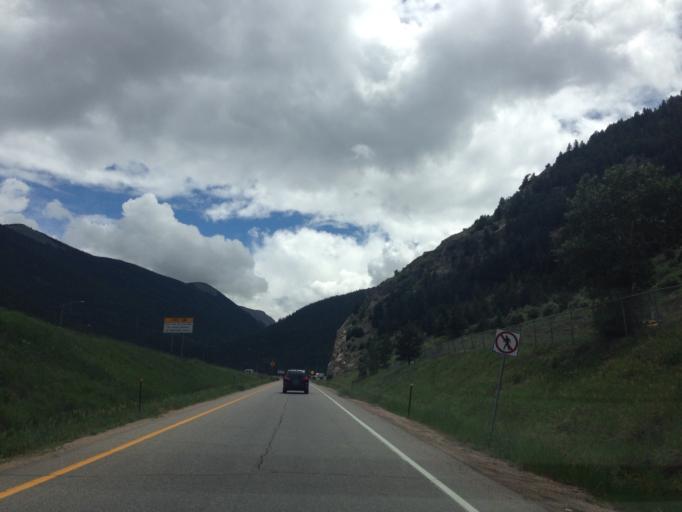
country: US
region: Colorado
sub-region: Clear Creek County
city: Georgetown
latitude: 39.7151
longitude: -105.6971
